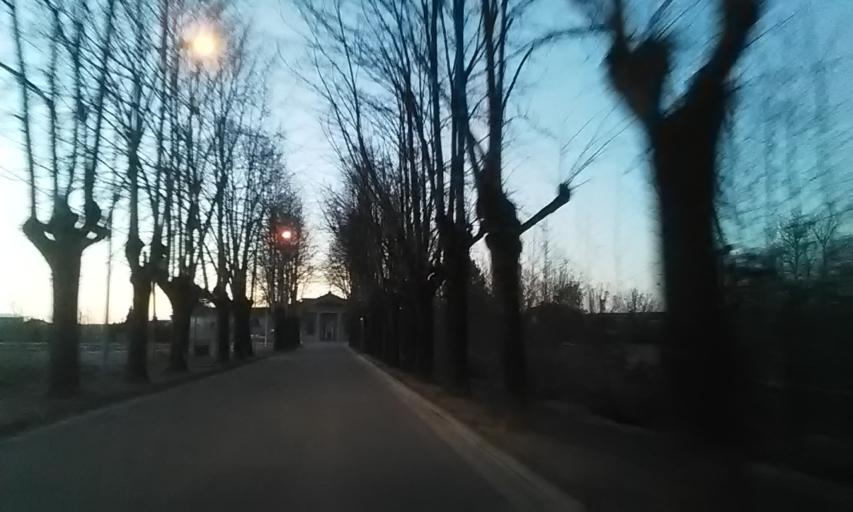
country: IT
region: Piedmont
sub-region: Provincia di Biella
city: Occhieppo Inferiore
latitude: 45.5521
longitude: 8.0371
